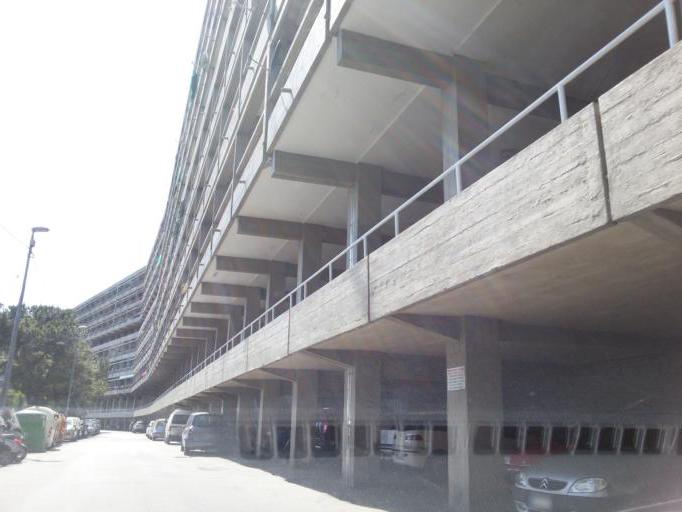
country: IT
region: Liguria
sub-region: Provincia di Genova
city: Genoa
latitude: 44.4253
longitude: 8.9604
